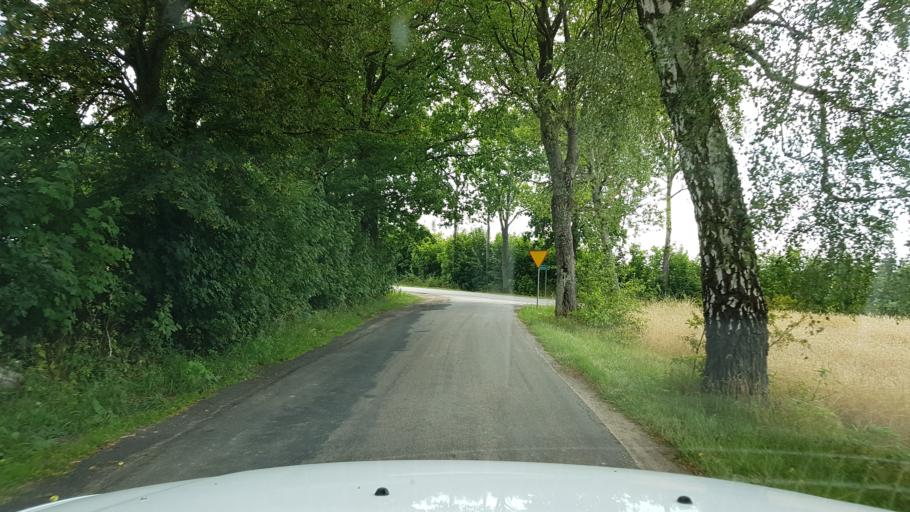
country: PL
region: West Pomeranian Voivodeship
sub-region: Koszalin
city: Koszalin
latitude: 54.1566
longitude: 16.0764
